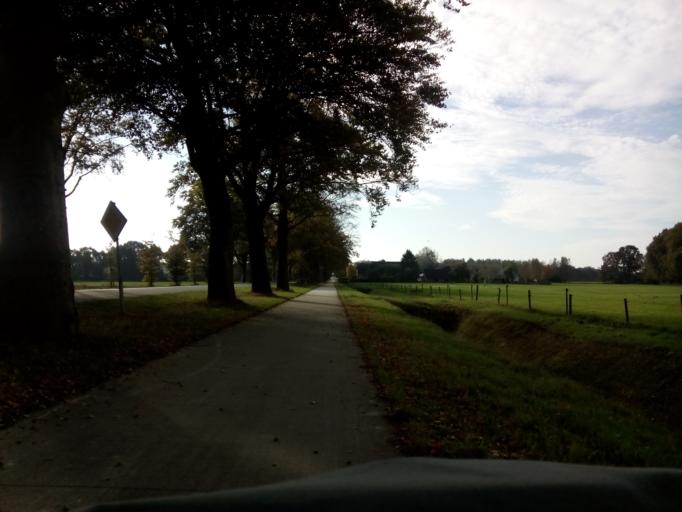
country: NL
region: Drenthe
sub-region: Gemeente Assen
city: Assen
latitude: 53.0342
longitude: 6.5712
